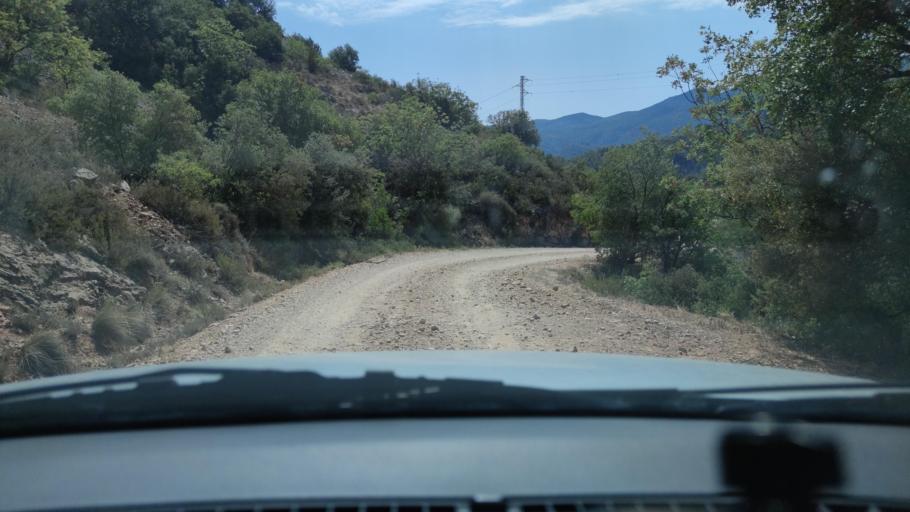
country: ES
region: Catalonia
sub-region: Provincia de Lleida
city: Camarasa
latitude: 41.9277
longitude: 0.8213
